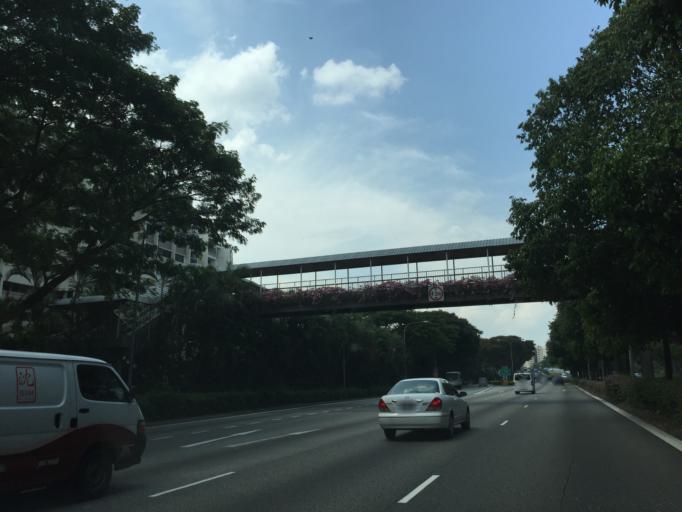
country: SG
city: Singapore
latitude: 1.3253
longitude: 103.9021
